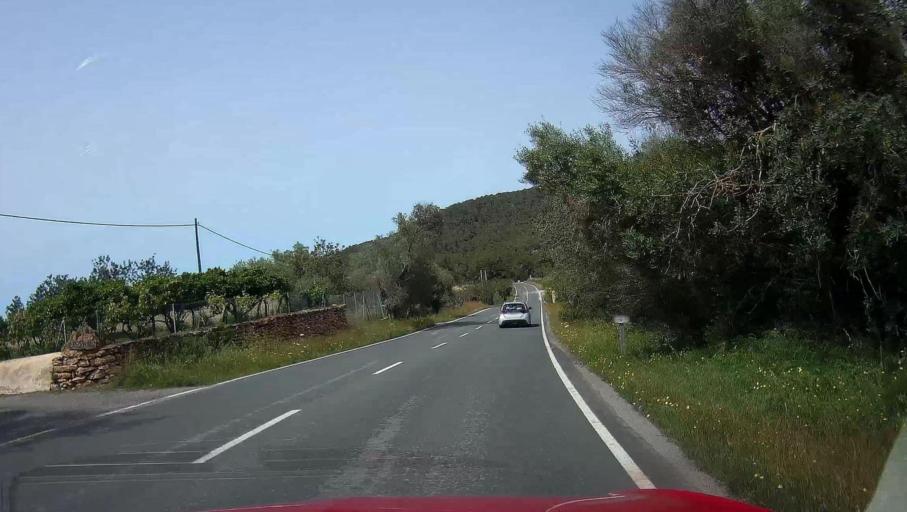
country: ES
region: Balearic Islands
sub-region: Illes Balears
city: Sant Joan de Labritja
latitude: 39.0879
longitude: 1.5018
